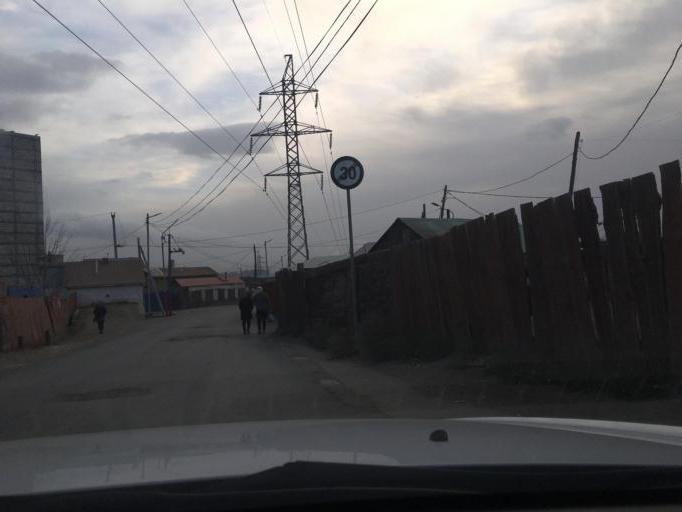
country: MN
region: Ulaanbaatar
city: Ulaanbaatar
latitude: 47.9239
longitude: 106.8584
